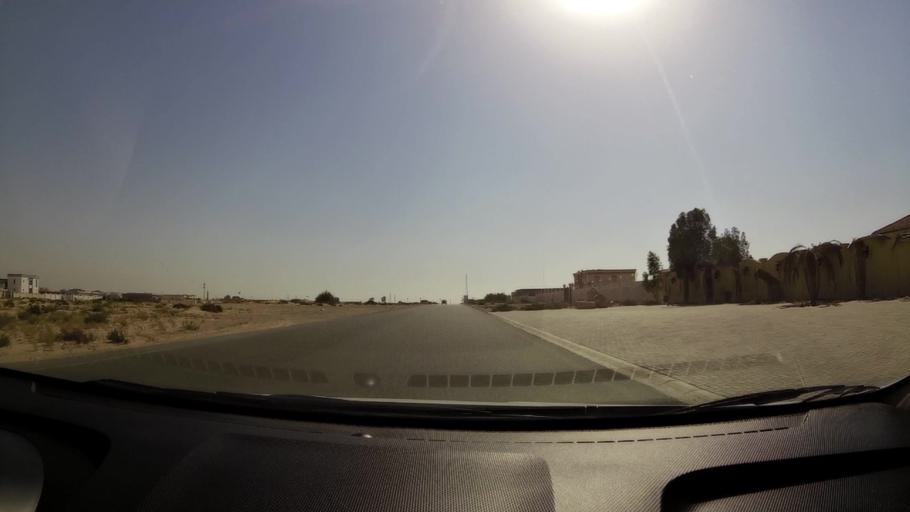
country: AE
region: Umm al Qaywayn
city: Umm al Qaywayn
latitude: 25.4901
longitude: 55.5924
